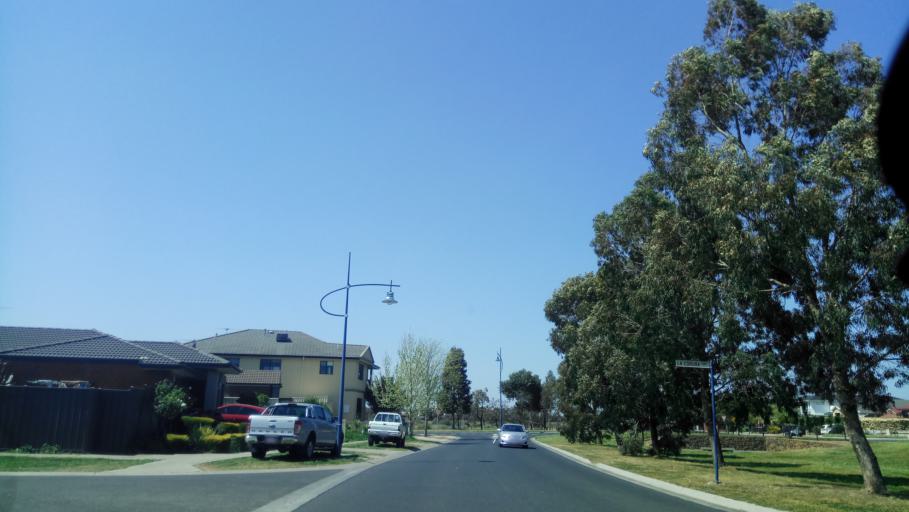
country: AU
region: Victoria
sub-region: Wyndham
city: Point Cook
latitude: -37.8946
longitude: 144.7395
